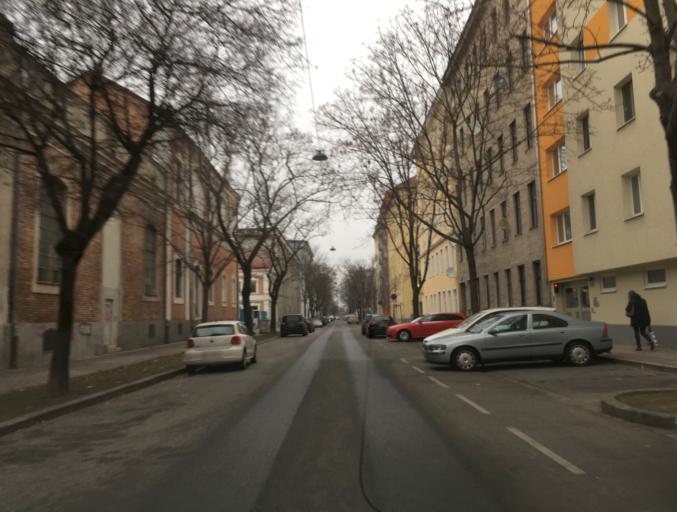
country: AT
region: Vienna
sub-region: Wien Stadt
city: Vienna
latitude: 48.2324
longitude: 16.3876
